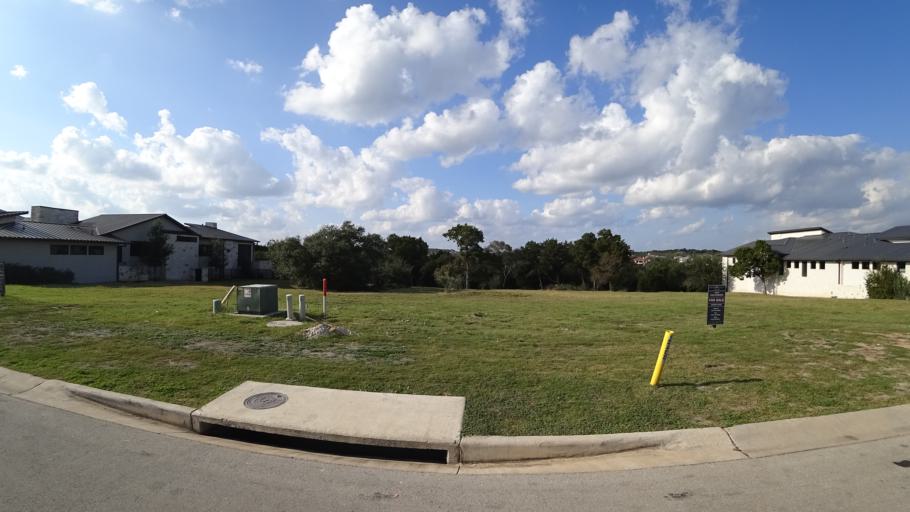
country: US
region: Texas
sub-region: Travis County
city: Barton Creek
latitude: 30.2733
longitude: -97.8753
